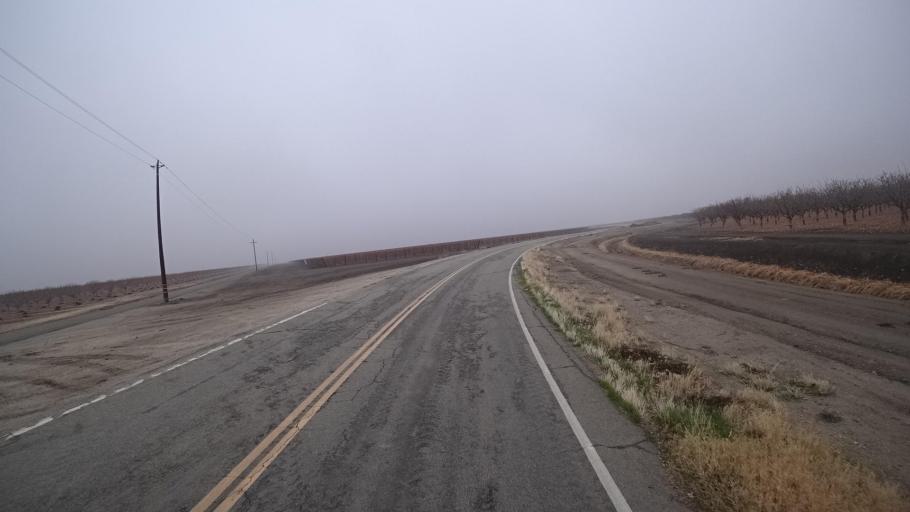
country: US
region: California
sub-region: Kern County
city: Buttonwillow
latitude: 35.4267
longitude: -119.5331
